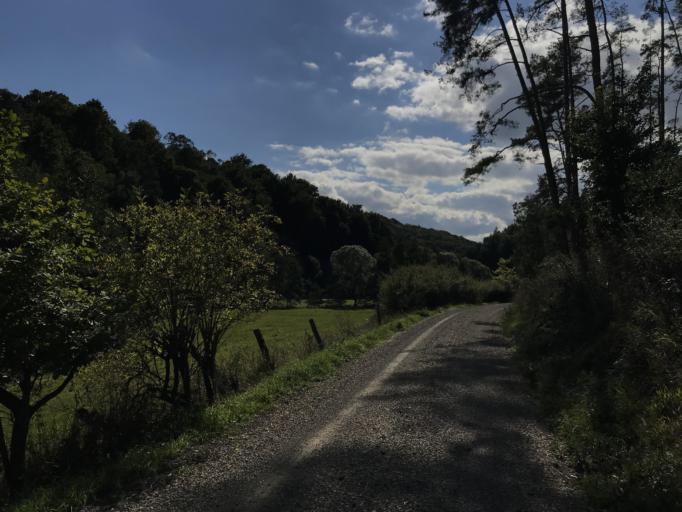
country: DE
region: Hesse
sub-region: Regierungsbezirk Kassel
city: Sachsenhausen
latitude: 51.2277
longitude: 9.0329
